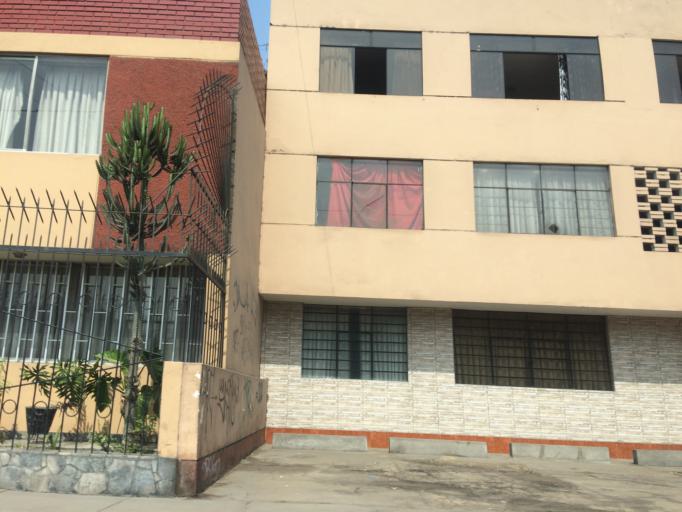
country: PE
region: Lima
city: Lima
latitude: -12.0242
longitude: -77.0366
